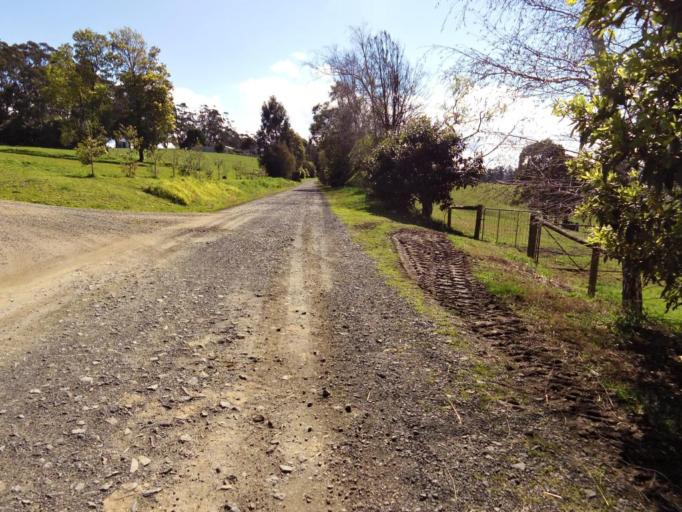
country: AU
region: Victoria
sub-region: Baw Baw
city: Warragul
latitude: -38.0396
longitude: 145.9529
